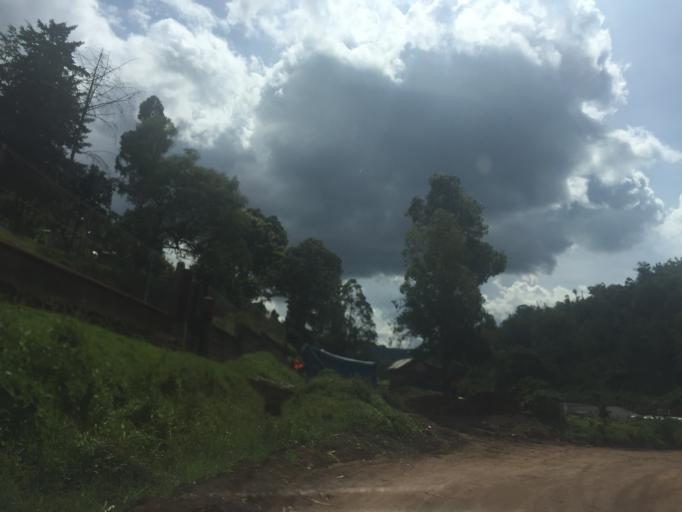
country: CD
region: South Kivu
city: Bukavu
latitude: -2.4616
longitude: 28.8372
